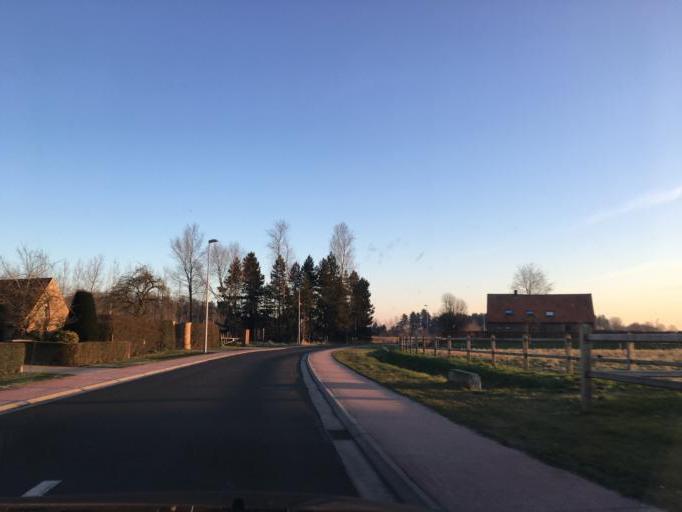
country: BE
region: Flanders
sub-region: Provincie Oost-Vlaanderen
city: Zomergem
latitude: 51.1447
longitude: 3.5656
